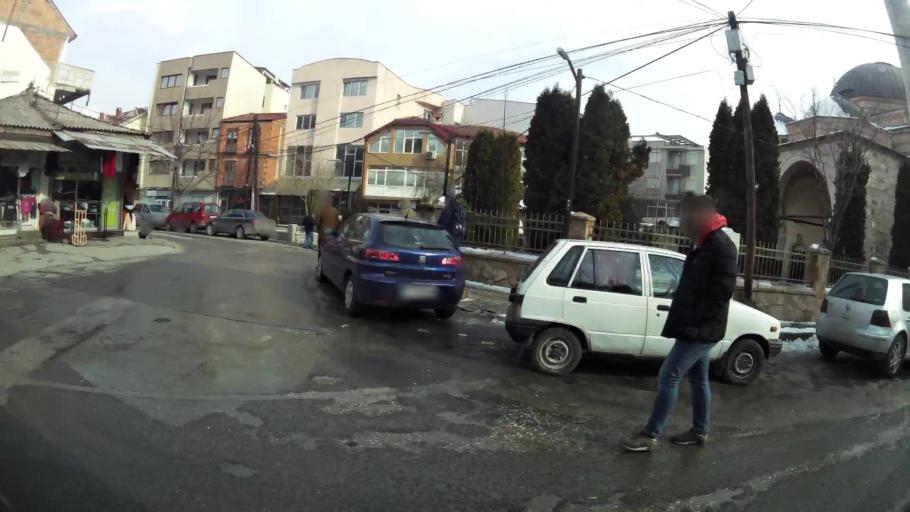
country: MK
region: Karpos
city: Skopje
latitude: 42.0061
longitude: 21.4353
